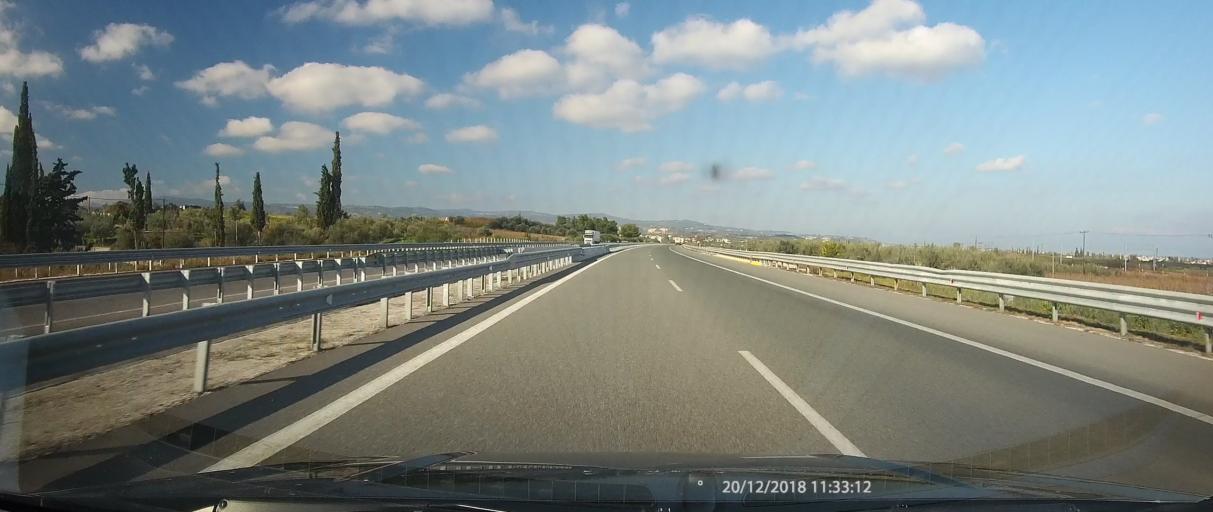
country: GR
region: Peloponnese
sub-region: Nomos Korinthias
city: Vokhaiko
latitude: 37.9402
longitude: 22.7670
